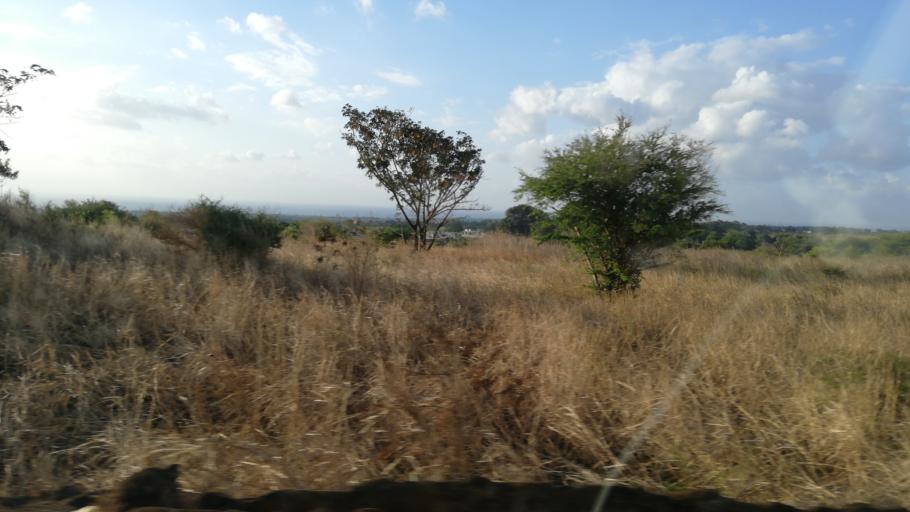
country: MU
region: Black River
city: Gros Cailloux
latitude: -20.2244
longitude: 57.4307
